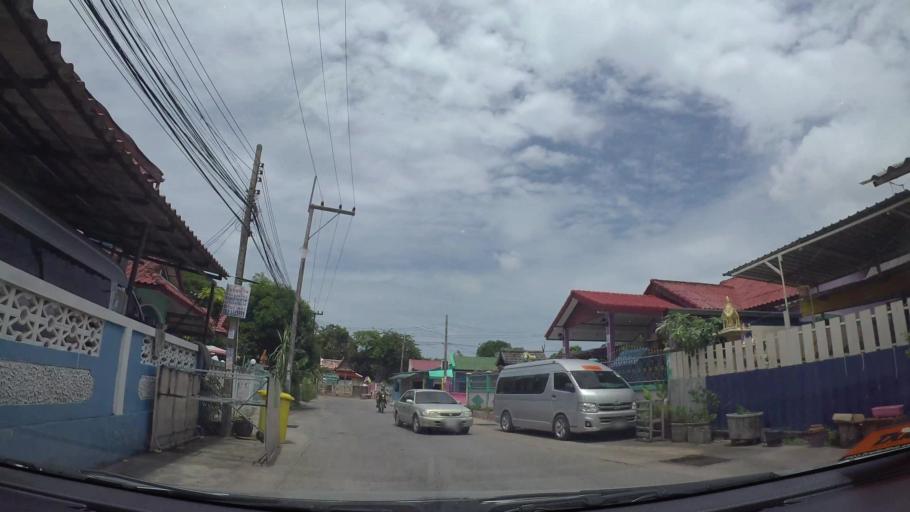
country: TH
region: Chon Buri
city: Sattahip
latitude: 12.6820
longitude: 100.9021
